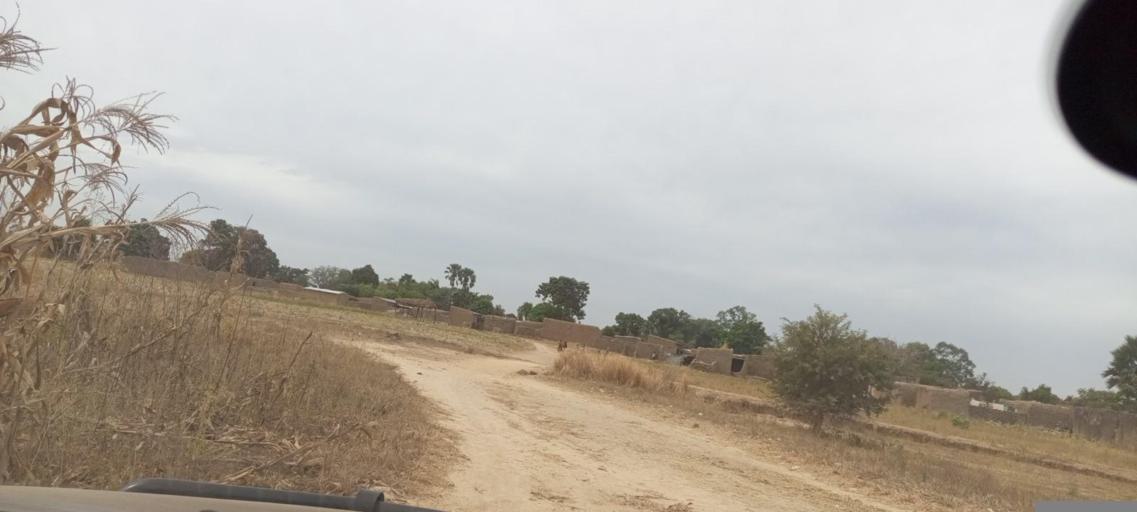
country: ML
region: Koulikoro
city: Kati
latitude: 12.7555
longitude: -8.3115
